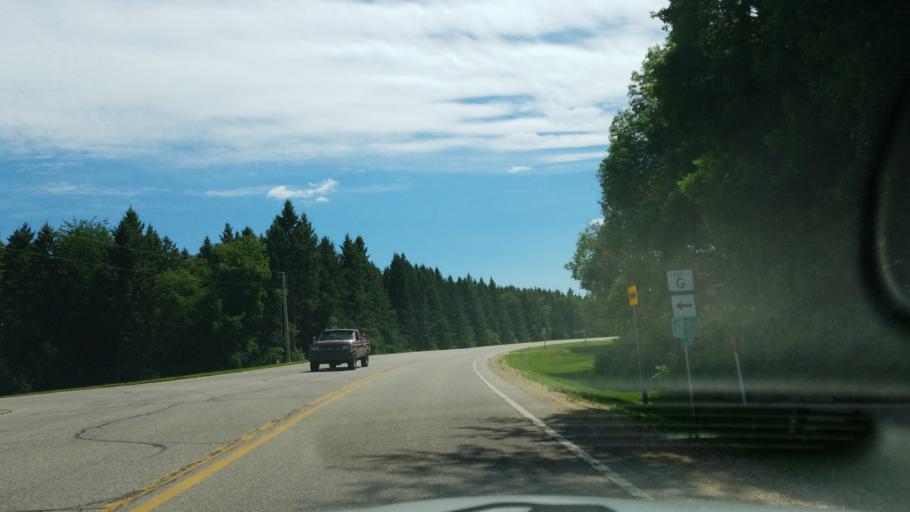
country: US
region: Wisconsin
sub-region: Saint Croix County
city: Glenwood City
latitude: 45.0467
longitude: -92.1743
